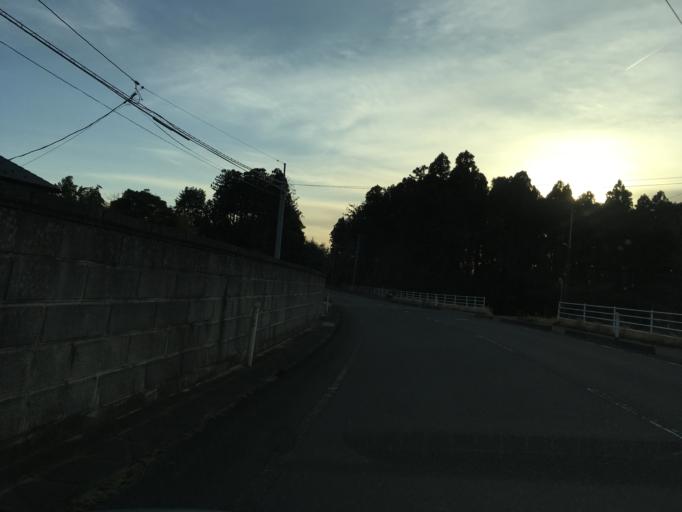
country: JP
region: Miyagi
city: Wakuya
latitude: 38.7043
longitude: 141.1168
